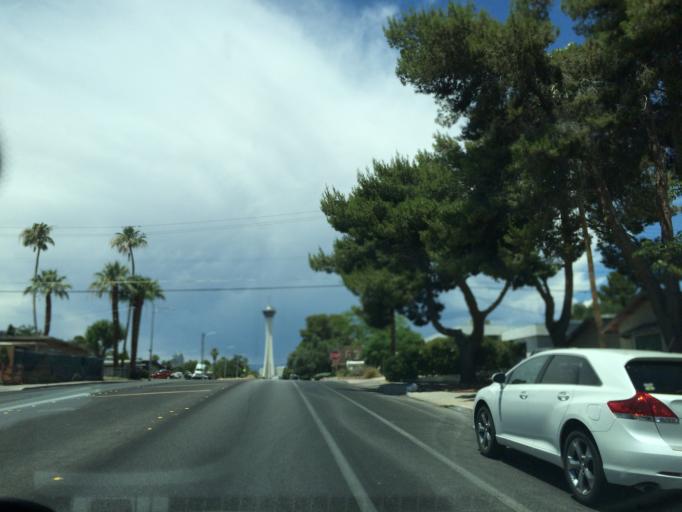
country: US
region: Nevada
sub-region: Clark County
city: Winchester
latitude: 36.1481
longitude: -115.1319
